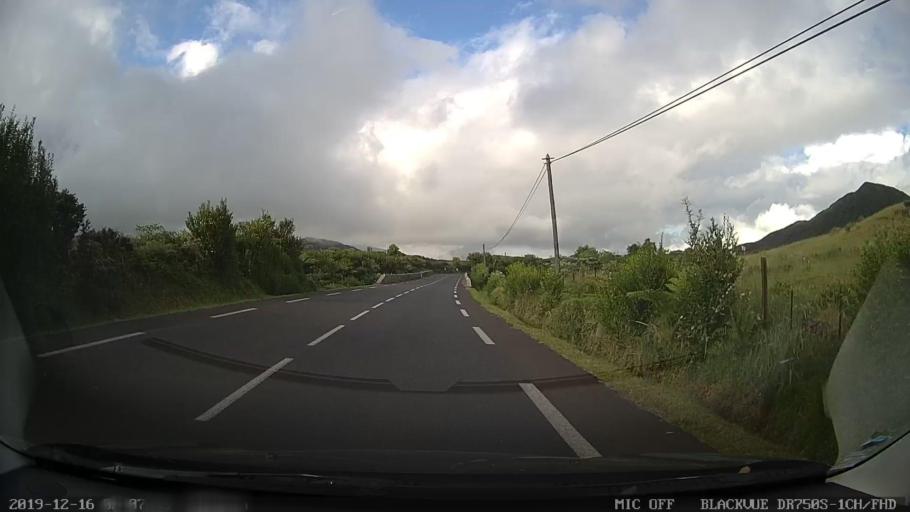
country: RE
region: Reunion
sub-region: Reunion
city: Cilaos
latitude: -21.1797
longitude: 55.5795
